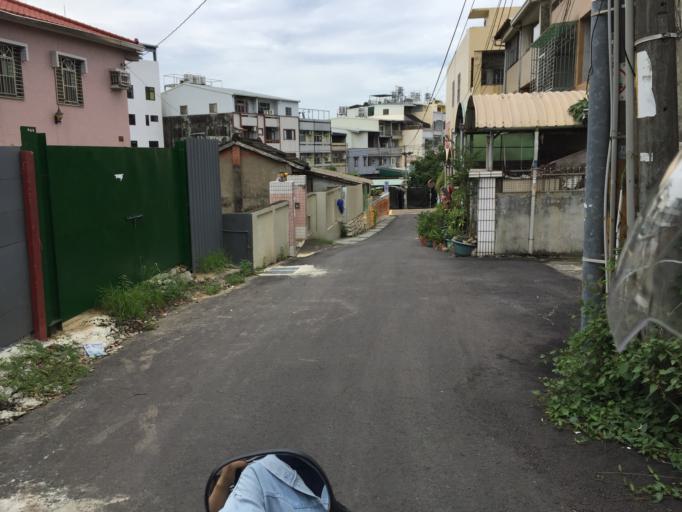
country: TW
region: Taiwan
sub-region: Taichung City
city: Taichung
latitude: 24.0648
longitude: 120.7035
